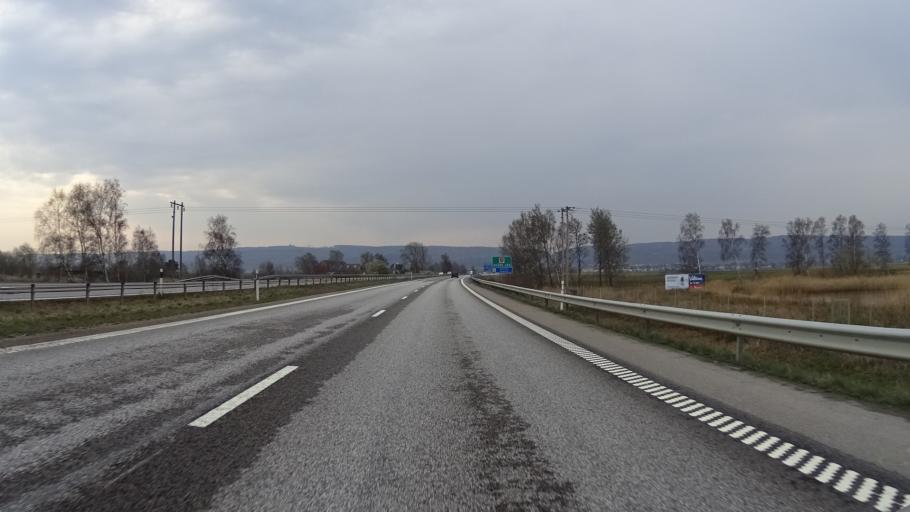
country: SE
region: Halland
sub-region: Laholms Kommun
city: Mellbystrand
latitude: 56.4427
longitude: 12.9541
